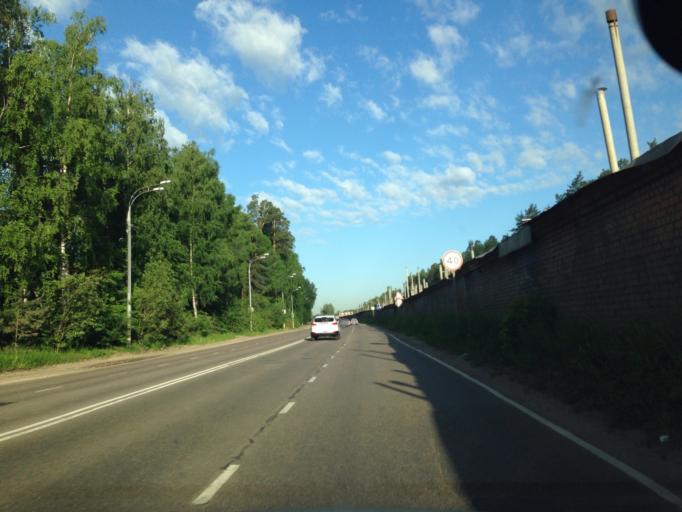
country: RU
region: Moskovskaya
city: Balashikha
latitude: 55.8062
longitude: 37.9342
